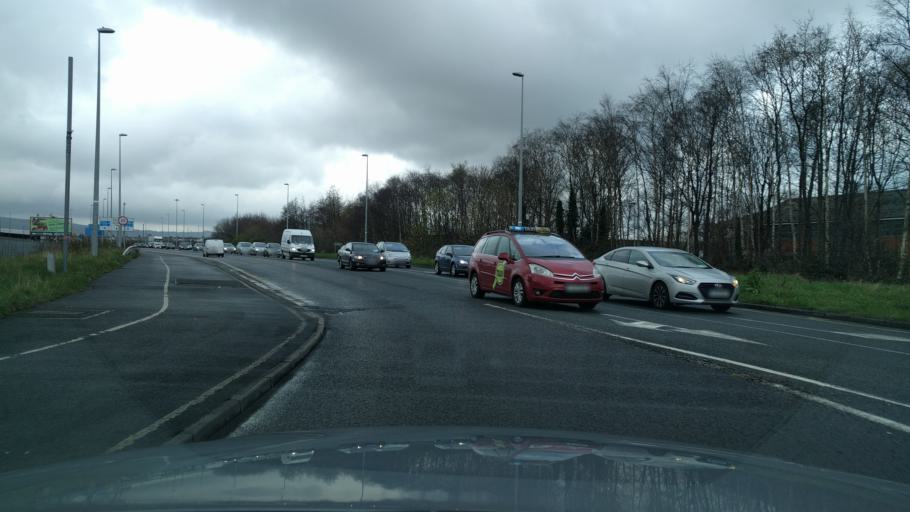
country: IE
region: Leinster
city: Crumlin
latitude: 53.3101
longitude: -6.3533
